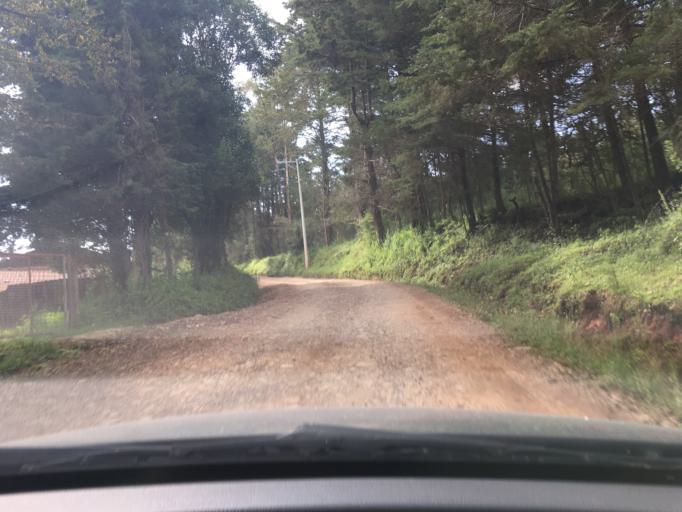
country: MX
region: Michoacan
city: Acuitzio del Canje
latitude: 19.5131
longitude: -101.2139
